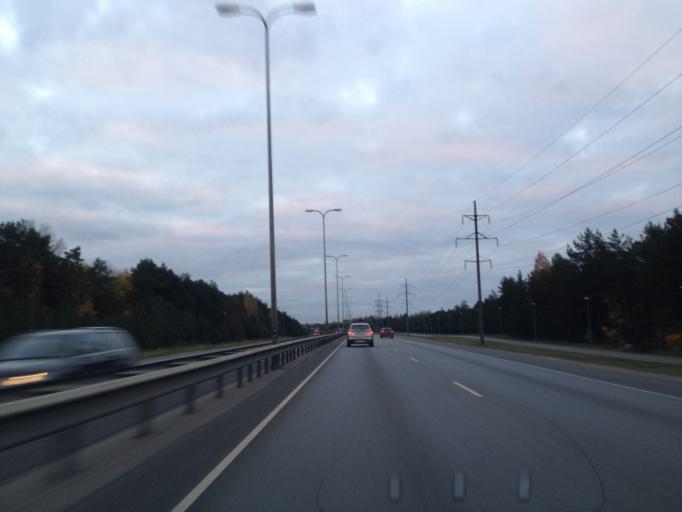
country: EE
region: Harju
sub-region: Tallinna linn
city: Tallinn
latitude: 59.4081
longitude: 24.7479
